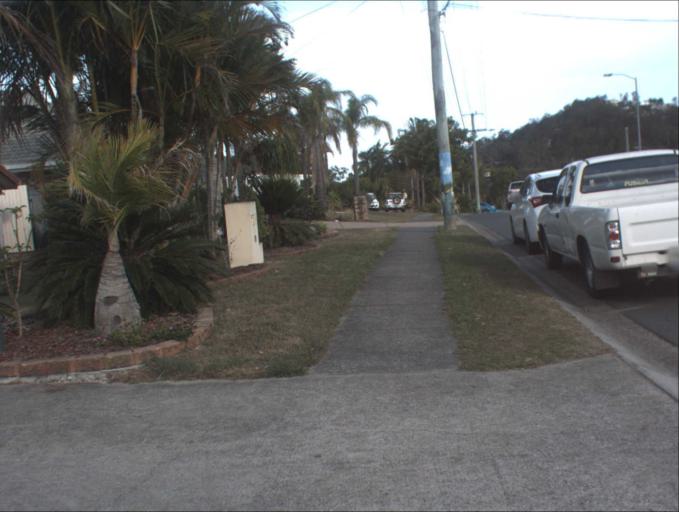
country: AU
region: Queensland
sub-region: Logan
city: Slacks Creek
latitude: -27.6517
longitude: 153.1866
